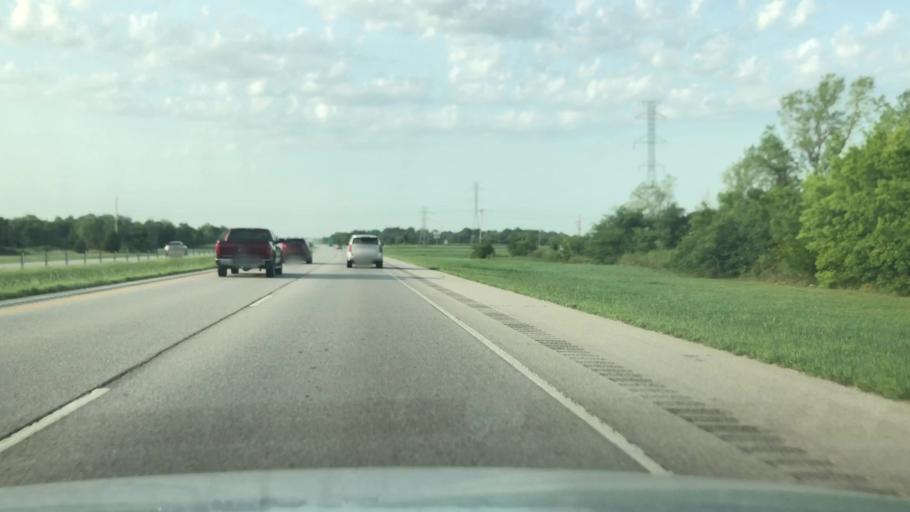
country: US
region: Oklahoma
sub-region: Tulsa County
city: Sperry
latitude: 36.2952
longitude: -95.9252
